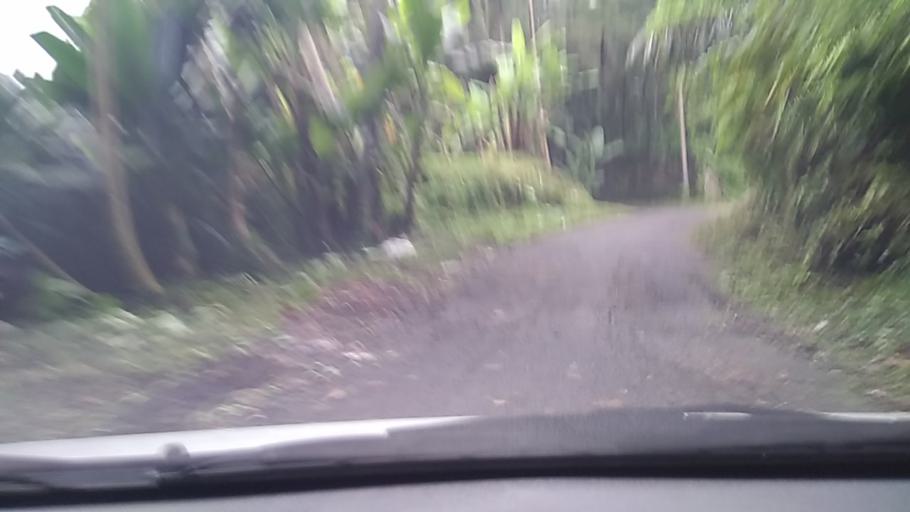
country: ID
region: Bali
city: Banjar Dujung Kaja
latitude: -8.4079
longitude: 115.2887
